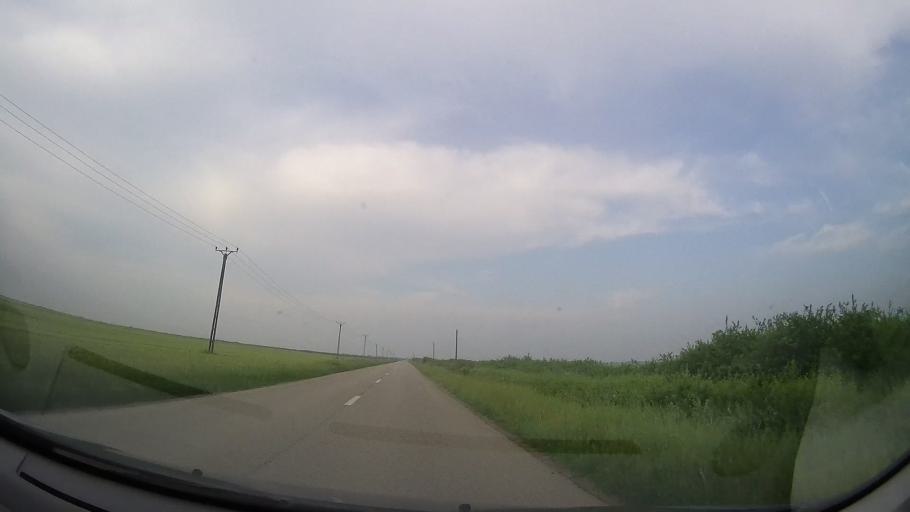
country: RO
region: Timis
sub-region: Comuna Foeni
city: Foeni
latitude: 45.5154
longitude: 20.8955
